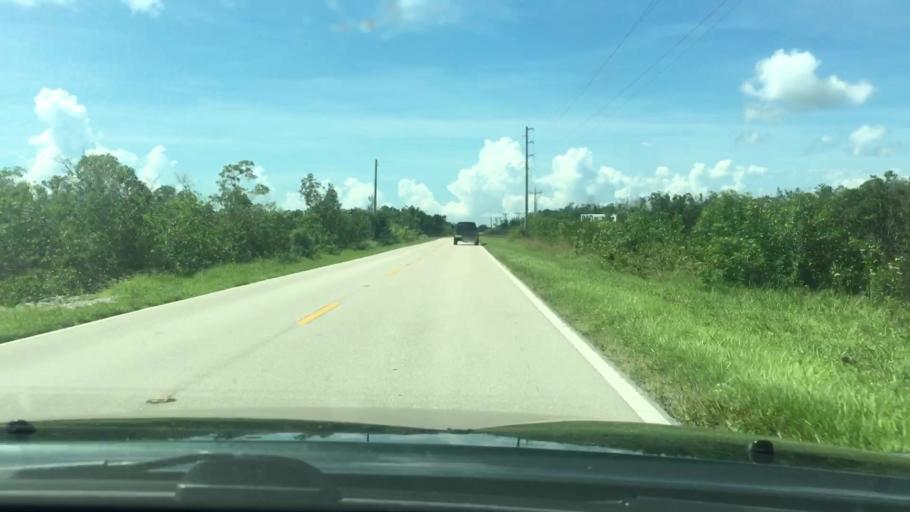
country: US
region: Florida
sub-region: Collier County
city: Marco
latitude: 25.9408
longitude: -81.6459
